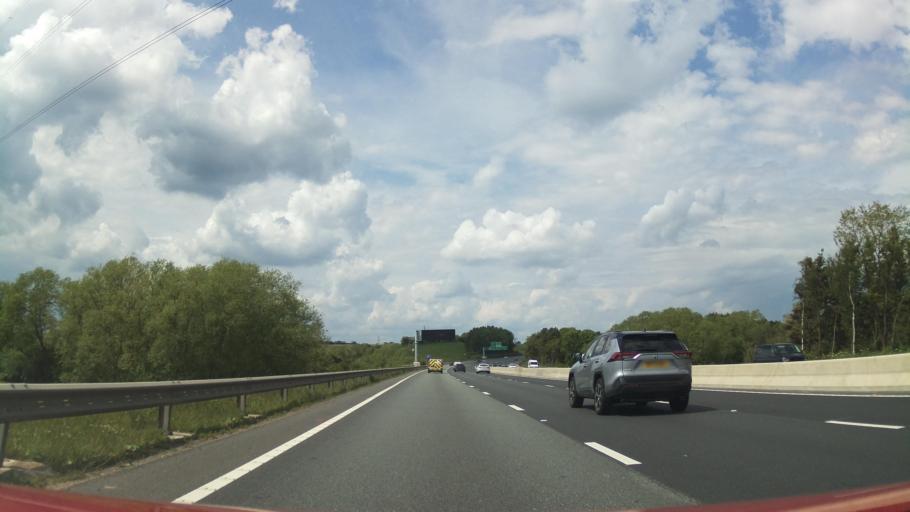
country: GB
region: England
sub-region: Stockton-on-Tees
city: Billingham
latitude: 54.6031
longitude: -1.3119
